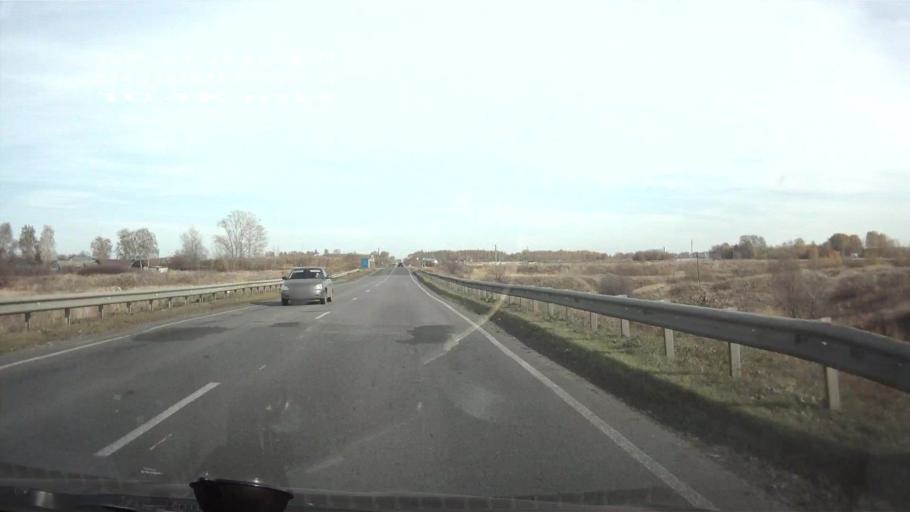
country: RU
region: Mordoviya
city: Atyashevo
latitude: 54.5553
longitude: 45.9656
